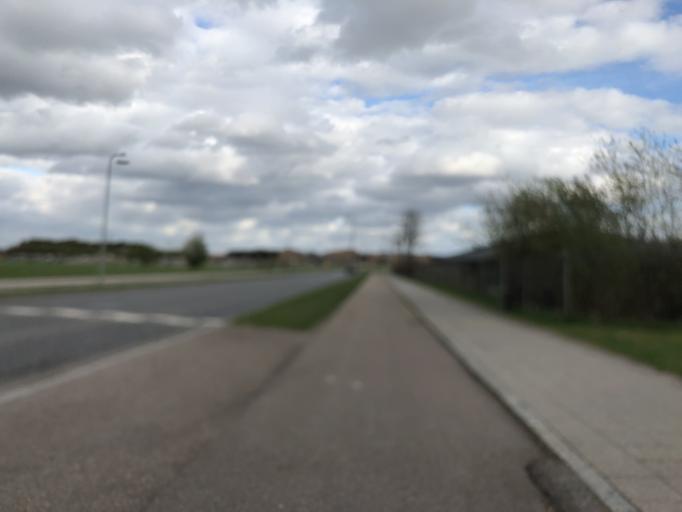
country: DK
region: Zealand
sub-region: Ringsted Kommune
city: Ringsted
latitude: 55.4508
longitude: 11.7982
